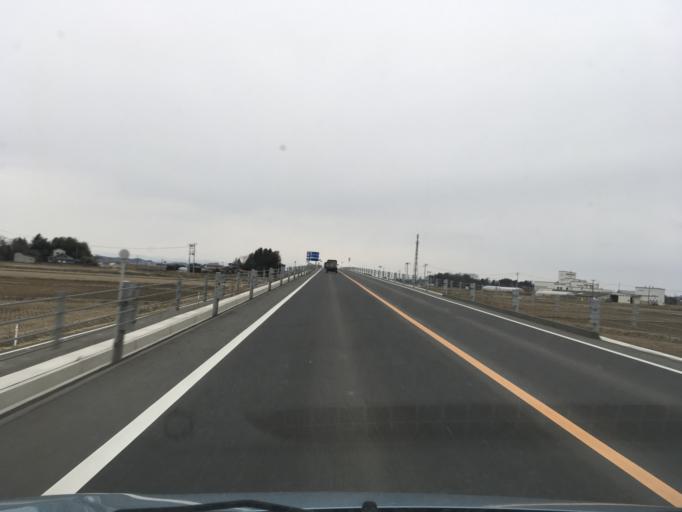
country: JP
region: Miyagi
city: Wakuya
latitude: 38.6820
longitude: 141.2531
